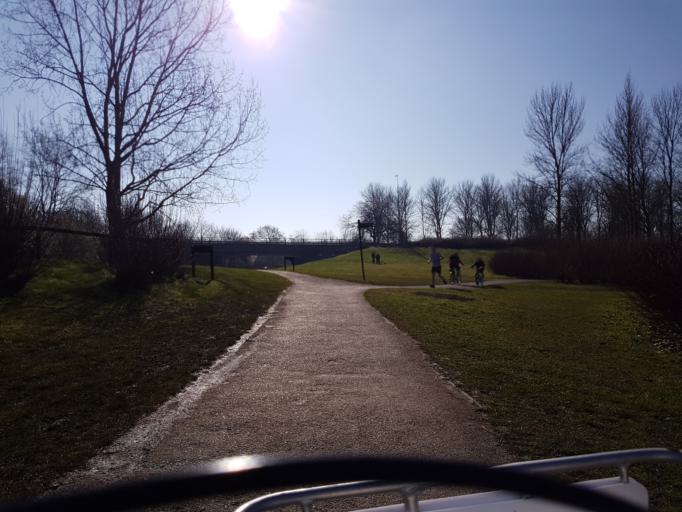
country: GB
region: England
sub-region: Milton Keynes
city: Broughton
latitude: 52.0481
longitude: -0.7140
